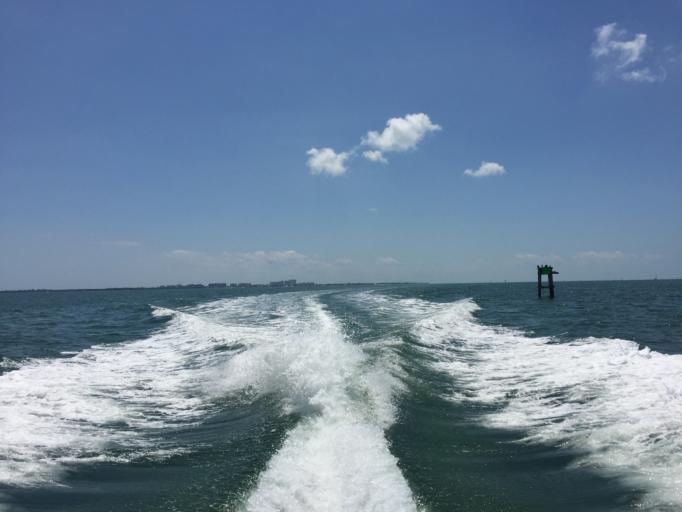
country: US
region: Florida
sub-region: Miami-Dade County
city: Coconut Grove
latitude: 25.7209
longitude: -80.2167
